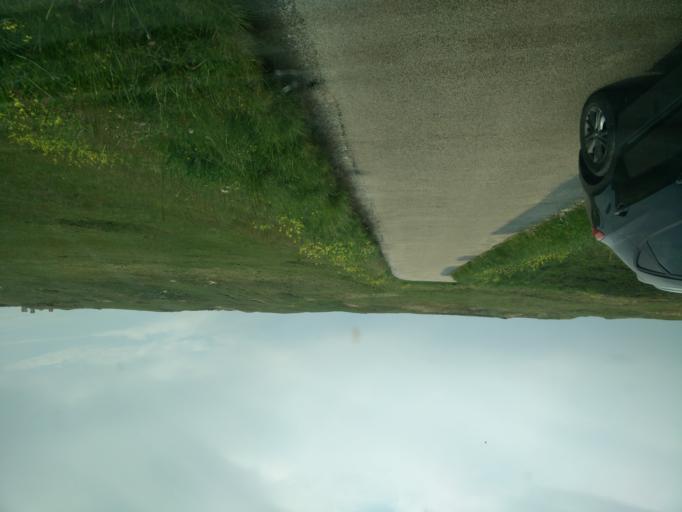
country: FR
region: Brittany
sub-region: Departement du Finistere
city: Camaret-sur-Mer
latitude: 48.2784
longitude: -4.6142
